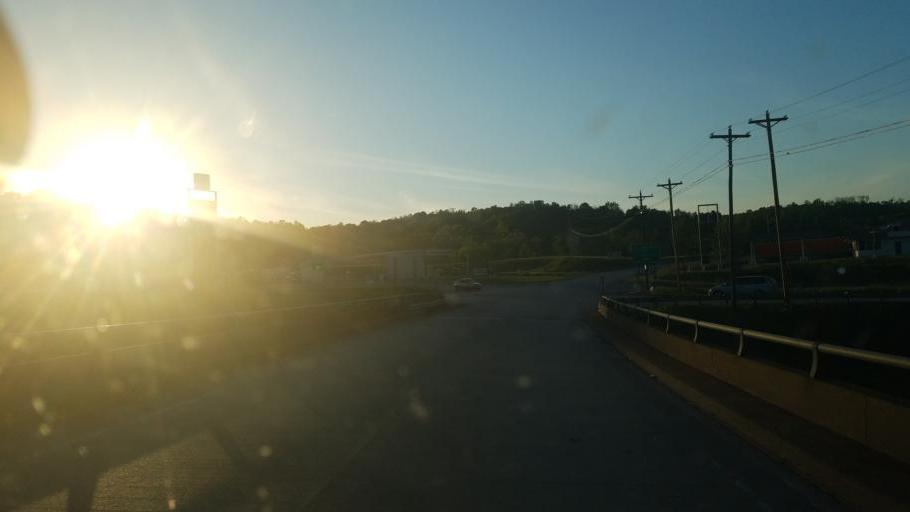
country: US
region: Ohio
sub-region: Belmont County
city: Barnesville
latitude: 40.0529
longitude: -81.3243
